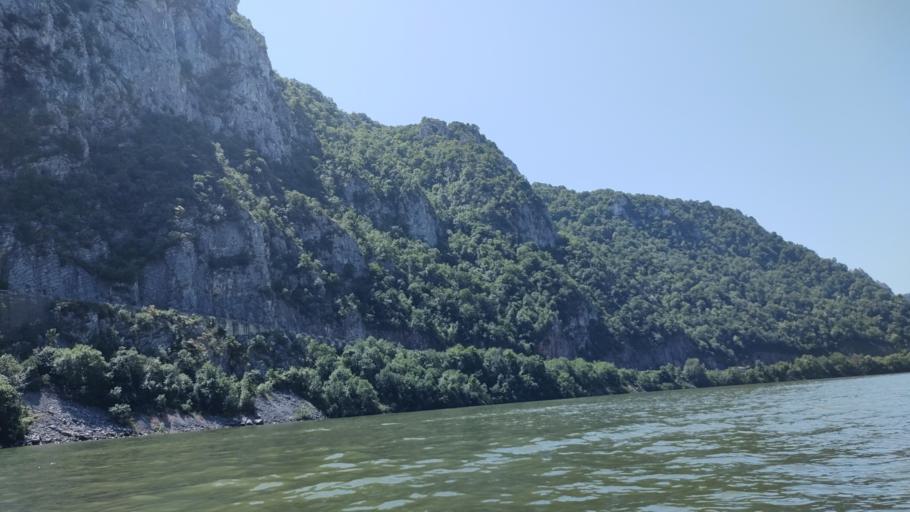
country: RO
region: Mehedinti
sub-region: Comuna Dubova
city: Dubova
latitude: 44.6325
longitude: 22.2884
